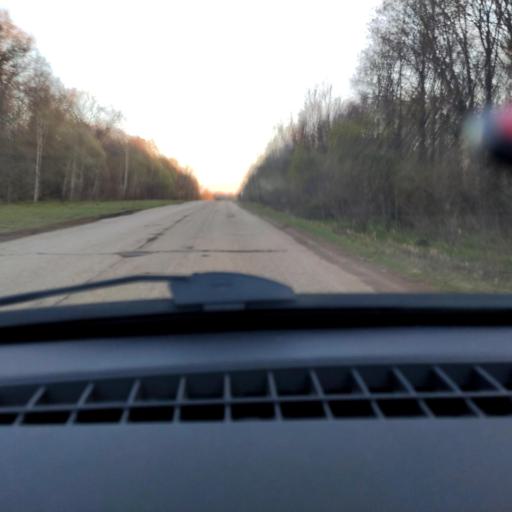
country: RU
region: Bashkortostan
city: Chishmy
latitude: 54.4526
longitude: 55.5463
